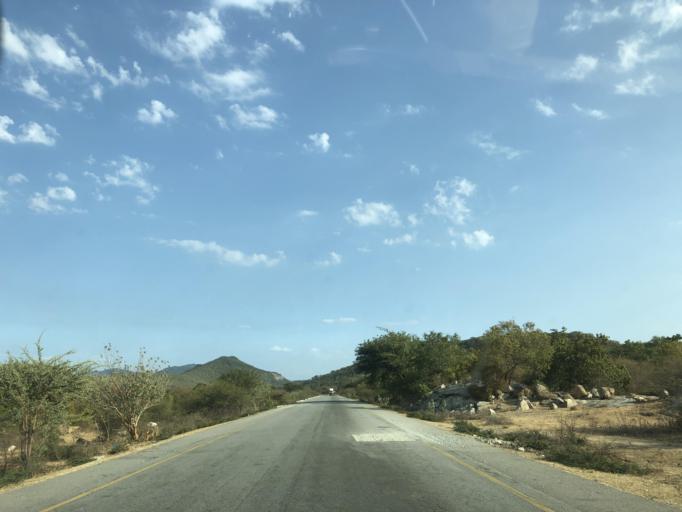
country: AO
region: Benguela
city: Benguela
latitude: -13.2552
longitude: 13.7819
